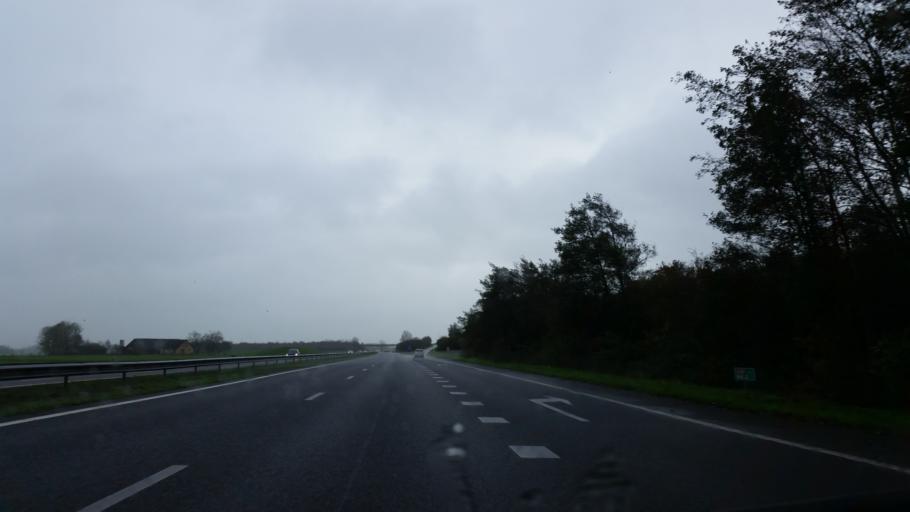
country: NL
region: Friesland
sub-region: Gemeente Boarnsterhim
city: Reduzum
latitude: 53.1180
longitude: 5.8093
